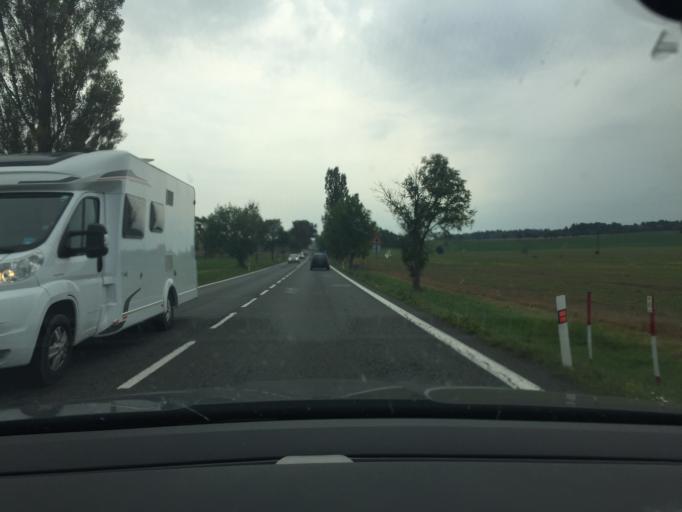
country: CZ
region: Central Bohemia
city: Milin
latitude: 49.6102
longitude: 14.0588
